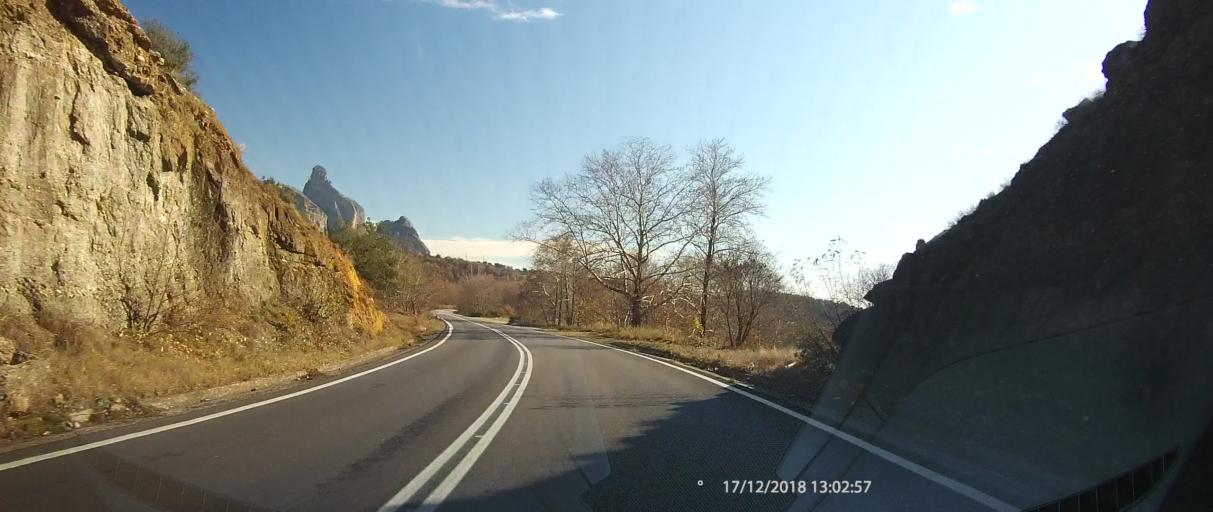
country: GR
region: Thessaly
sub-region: Trikala
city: Kastraki
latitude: 39.7170
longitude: 21.5969
